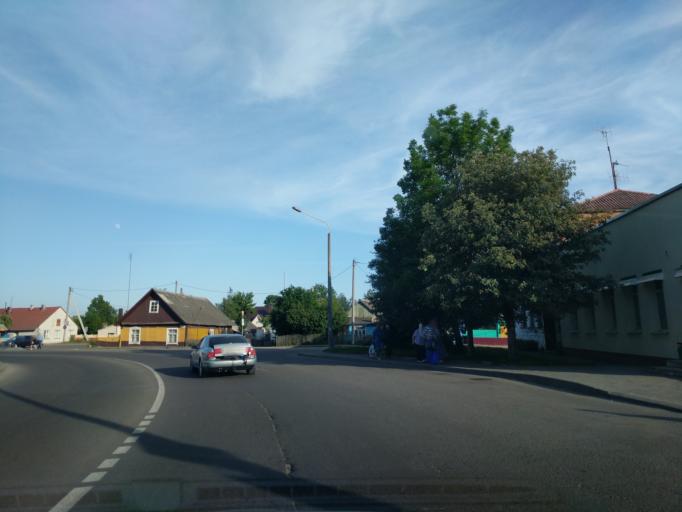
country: BY
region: Grodnenskaya
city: Ashmyany
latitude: 54.4237
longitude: 25.9305
